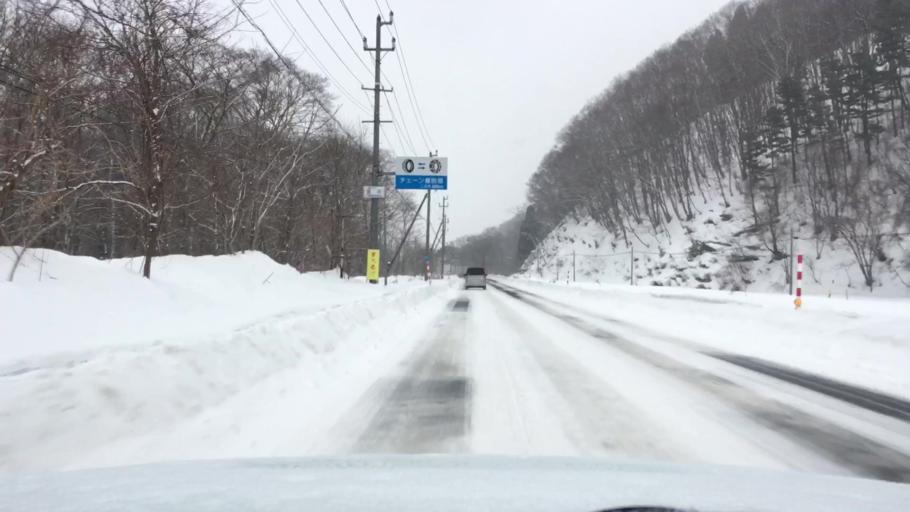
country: JP
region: Akita
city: Hanawa
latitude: 40.0403
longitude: 140.9961
